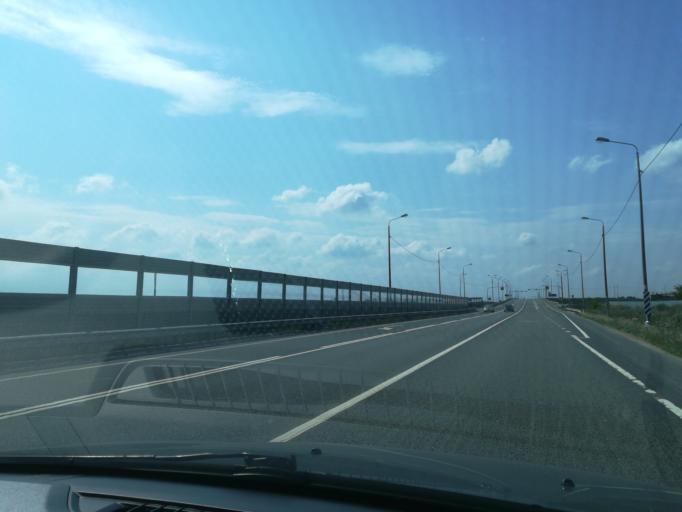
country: RU
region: Leningrad
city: Kingisepp
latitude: 59.5737
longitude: 28.7752
